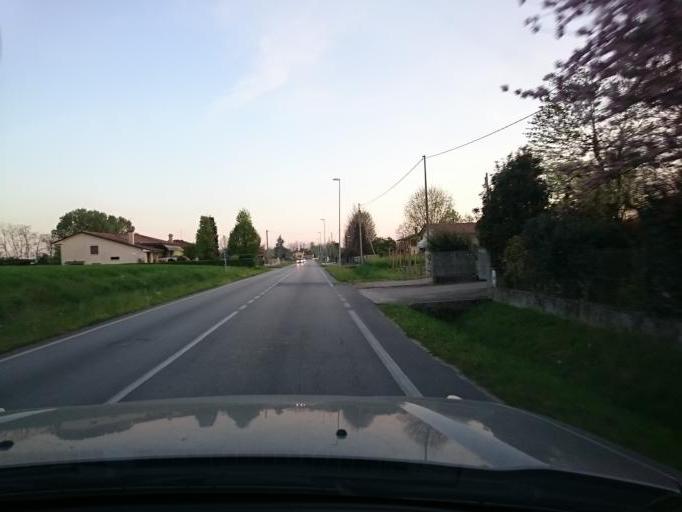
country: IT
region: Veneto
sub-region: Provincia di Treviso
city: Badoere
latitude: 45.6446
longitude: 12.1049
